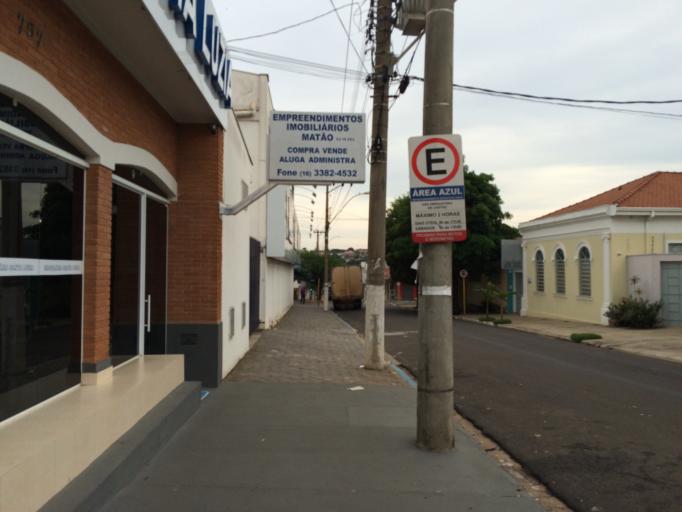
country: BR
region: Sao Paulo
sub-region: Matao
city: Matao
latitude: -21.6039
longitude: -48.3647
